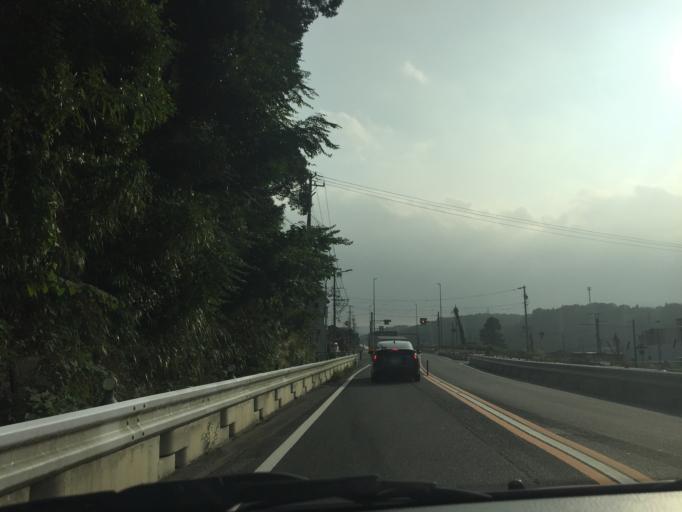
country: JP
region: Aichi
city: Shinshiro
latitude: 34.9226
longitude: 137.5379
